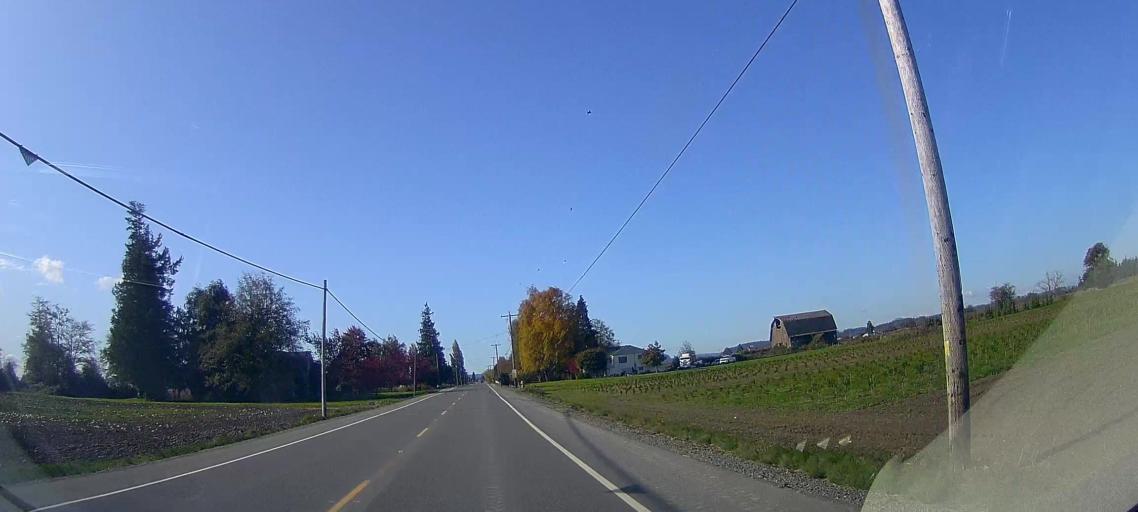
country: US
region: Washington
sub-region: Skagit County
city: Mount Vernon
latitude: 48.3406
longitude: -122.3811
